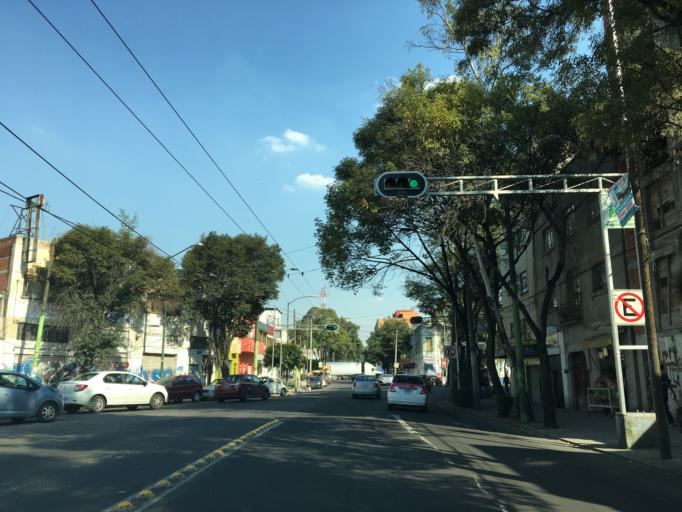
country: MX
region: Mexico City
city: Mexico City
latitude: 19.4148
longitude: -99.1379
